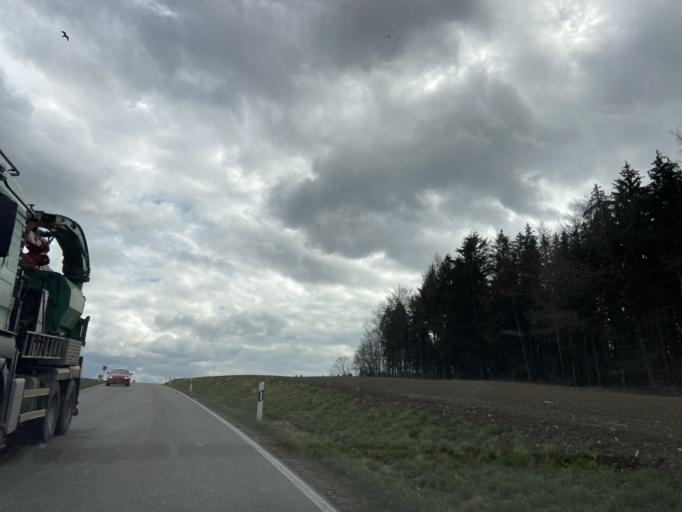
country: DE
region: Baden-Wuerttemberg
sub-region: Tuebingen Region
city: Konigseggwald
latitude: 47.9342
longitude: 9.4100
